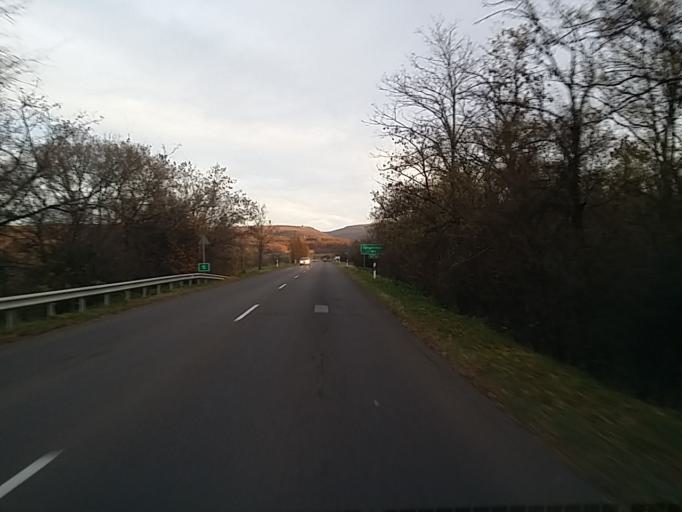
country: HU
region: Heves
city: Gyongyossolymos
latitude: 47.8130
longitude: 19.9579
